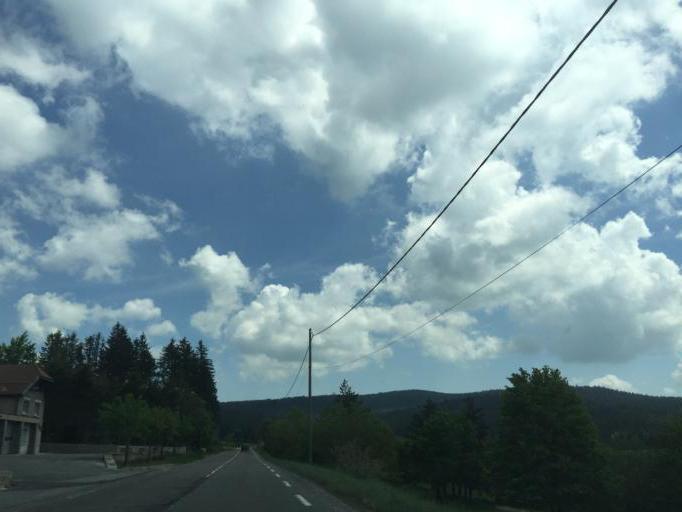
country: FR
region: Rhone-Alpes
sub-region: Departement de la Loire
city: Saint-Genest-Malifaux
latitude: 45.3521
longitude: 4.4711
